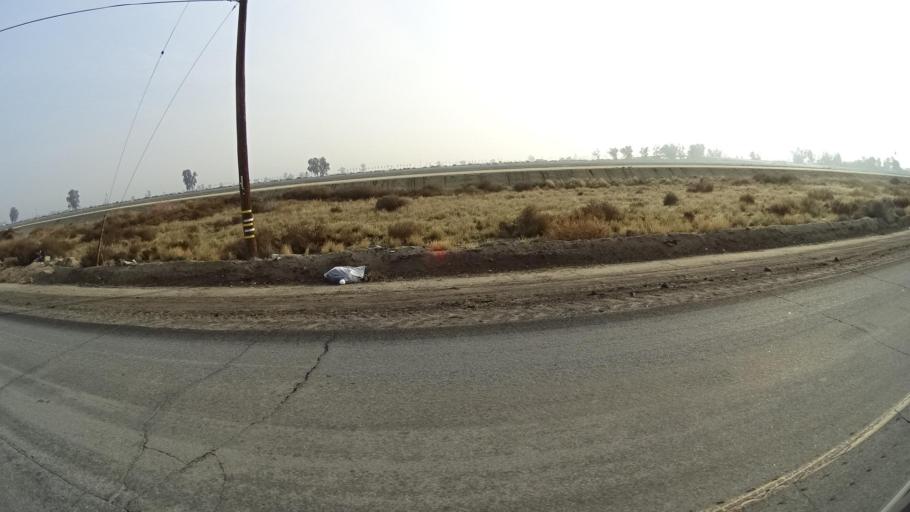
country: US
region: California
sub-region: Kern County
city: Greenfield
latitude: 35.2405
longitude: -119.0215
